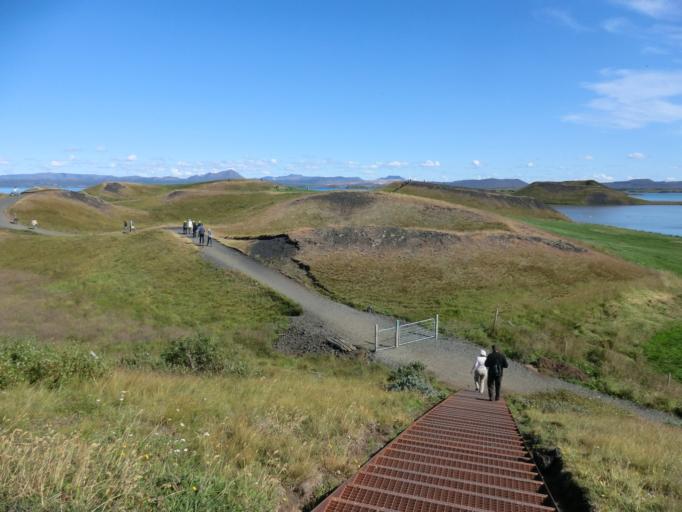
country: IS
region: Northeast
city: Laugar
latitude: 65.5693
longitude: -17.0367
